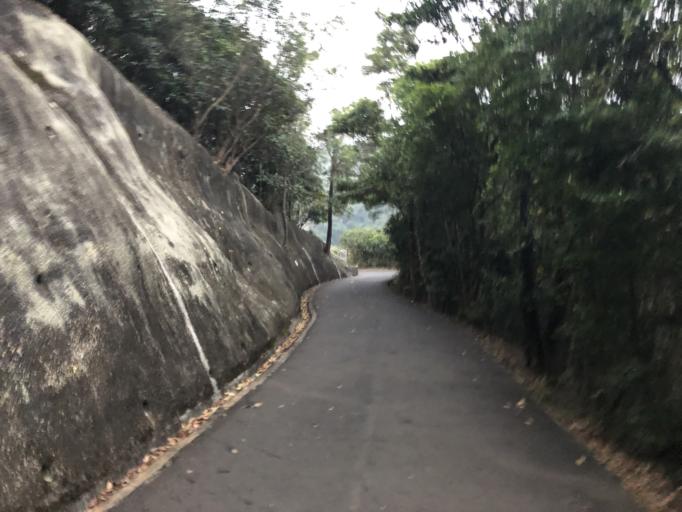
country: HK
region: Wanchai
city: Wan Chai
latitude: 22.2594
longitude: 114.2117
